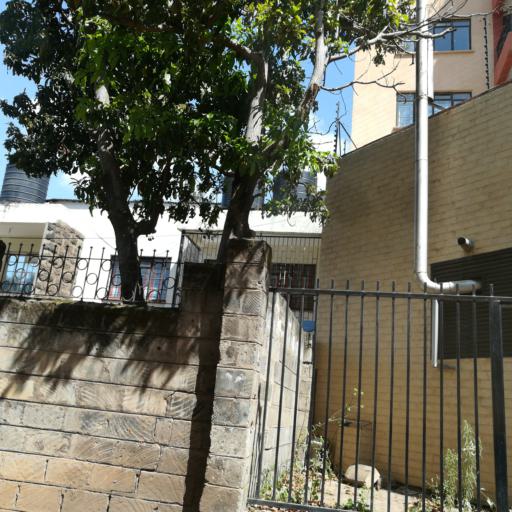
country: KE
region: Nairobi Area
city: Nairobi
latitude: -1.2952
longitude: 36.7978
